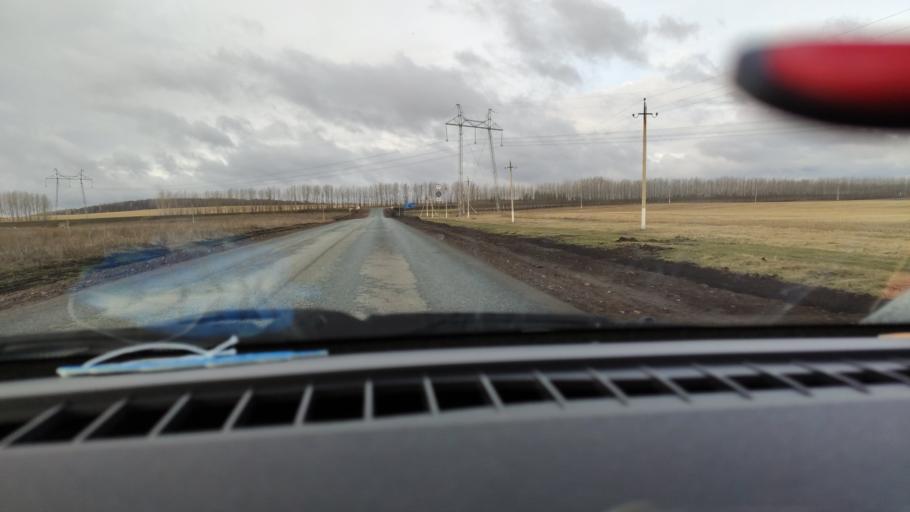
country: RU
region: Tatarstan
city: Russkiy Aktash
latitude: 55.0041
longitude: 51.7924
